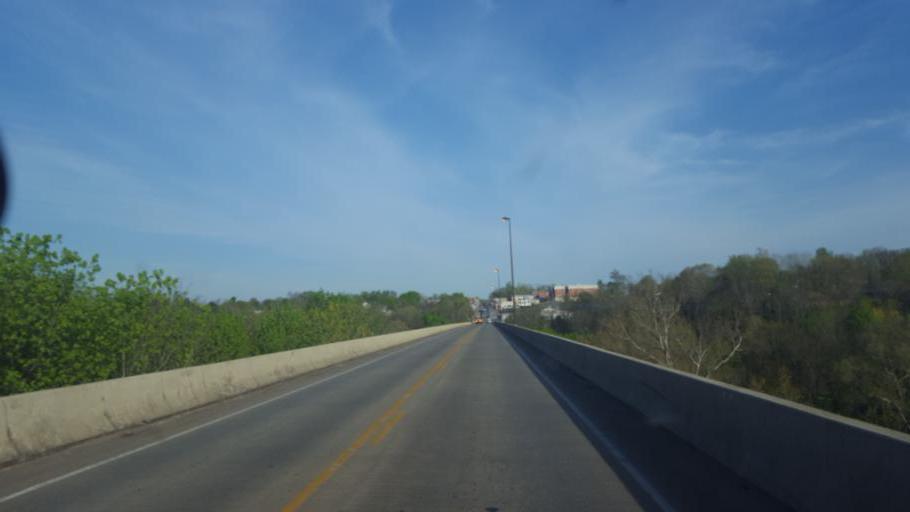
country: US
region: Kentucky
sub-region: Hart County
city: Munfordville
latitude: 37.2679
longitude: -85.8841
